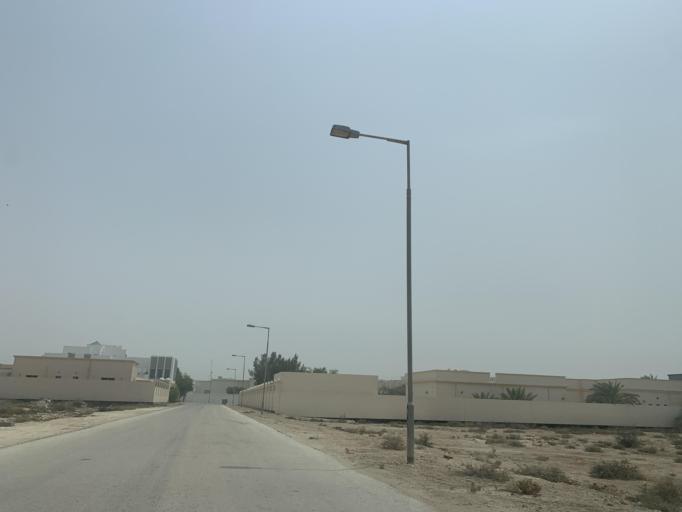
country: BH
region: Central Governorate
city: Madinat Hamad
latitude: 26.1618
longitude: 50.4787
